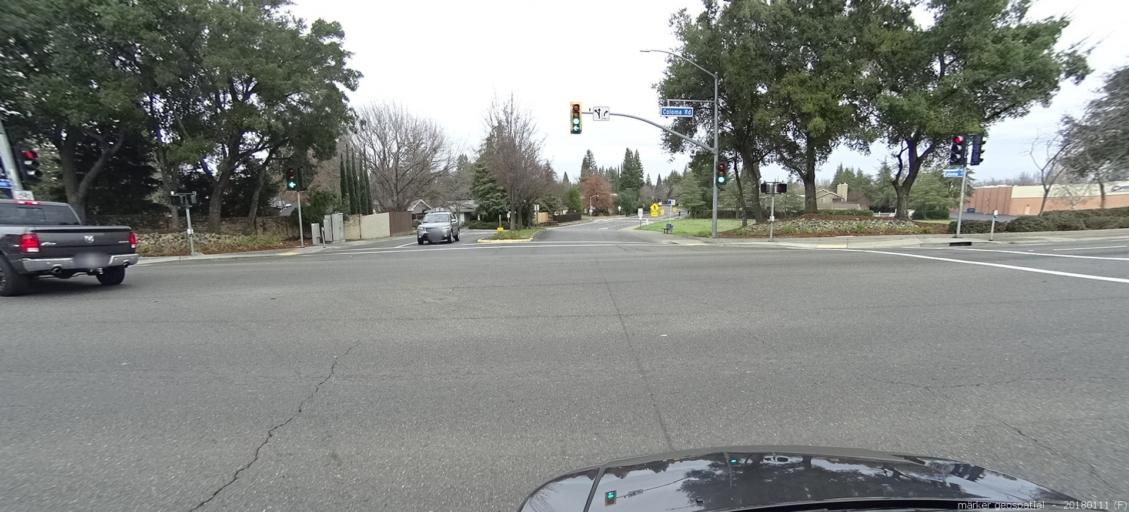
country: US
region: California
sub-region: Sacramento County
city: Gold River
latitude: 38.6179
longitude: -121.2708
